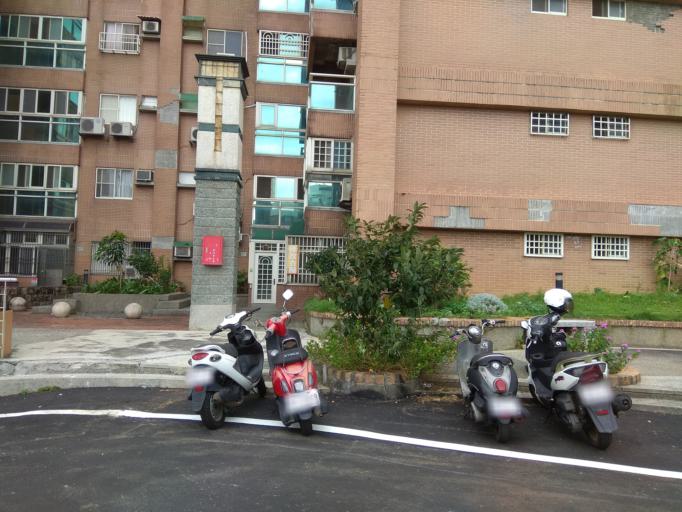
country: TW
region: Taiwan
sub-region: Hsinchu
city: Hsinchu
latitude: 24.7639
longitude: 120.9784
